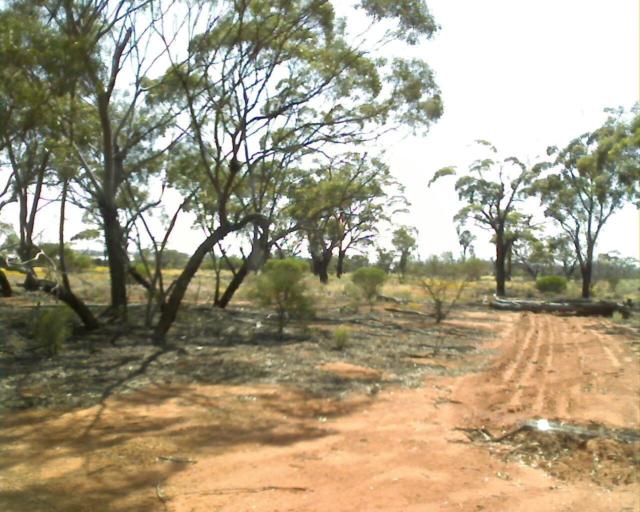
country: AU
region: Western Australia
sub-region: Merredin
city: Merredin
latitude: -30.9585
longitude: 118.8837
